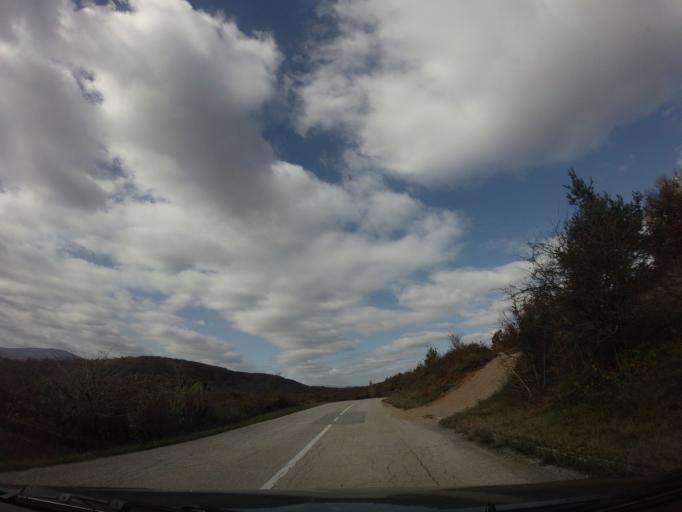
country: HR
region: Karlovacka
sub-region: Grad Karlovac
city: Slunj
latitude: 45.1649
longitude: 15.4932
